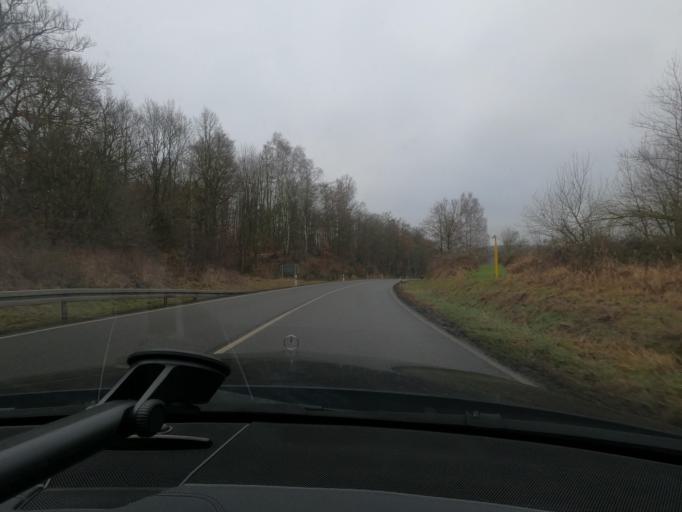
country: DE
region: Hesse
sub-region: Regierungsbezirk Kassel
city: Bad Arolsen
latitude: 51.3686
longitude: 9.0513
